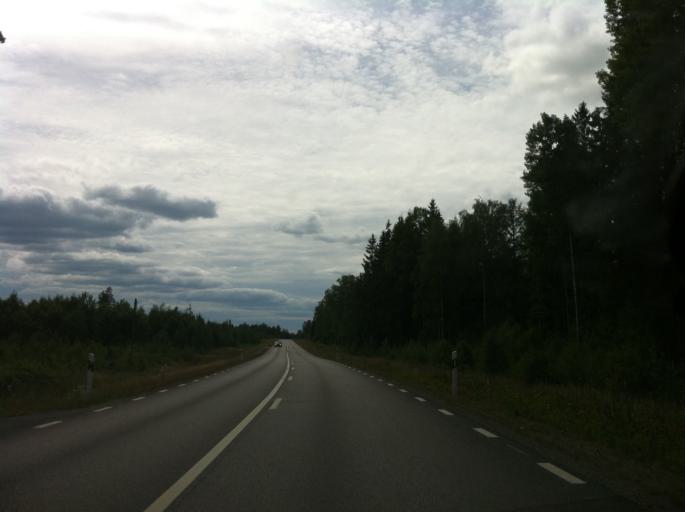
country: SE
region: Kronoberg
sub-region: Tingsryds Kommun
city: Tingsryd
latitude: 56.5038
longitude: 15.0977
